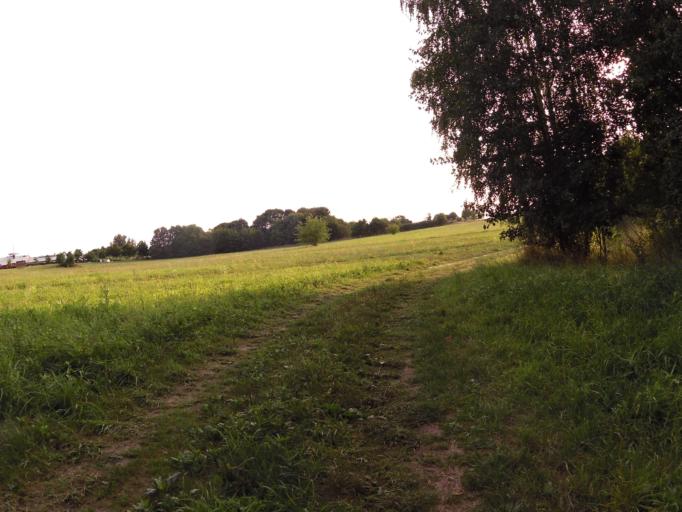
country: DE
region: Mecklenburg-Vorpommern
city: Seebad Bansin
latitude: 53.9638
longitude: 14.1440
